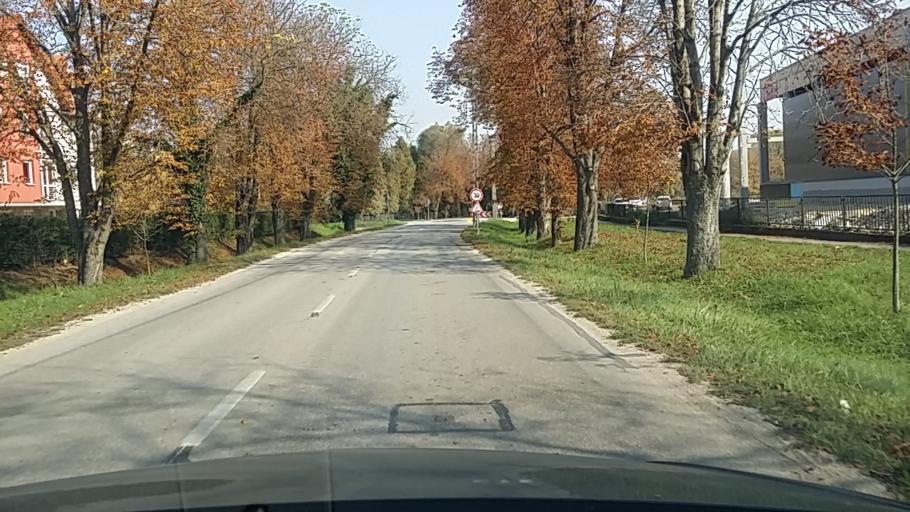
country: HU
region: Komarom-Esztergom
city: Tata
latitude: 47.6517
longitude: 18.3126
